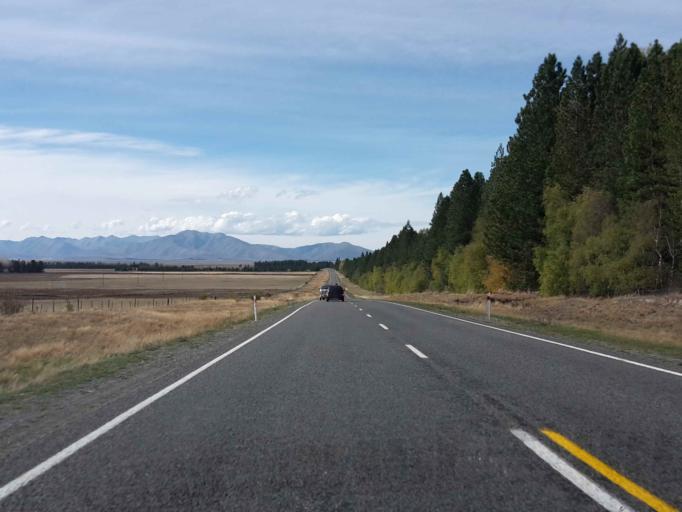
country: NZ
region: Canterbury
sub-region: Timaru District
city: Pleasant Point
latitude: -44.1937
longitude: 170.2863
